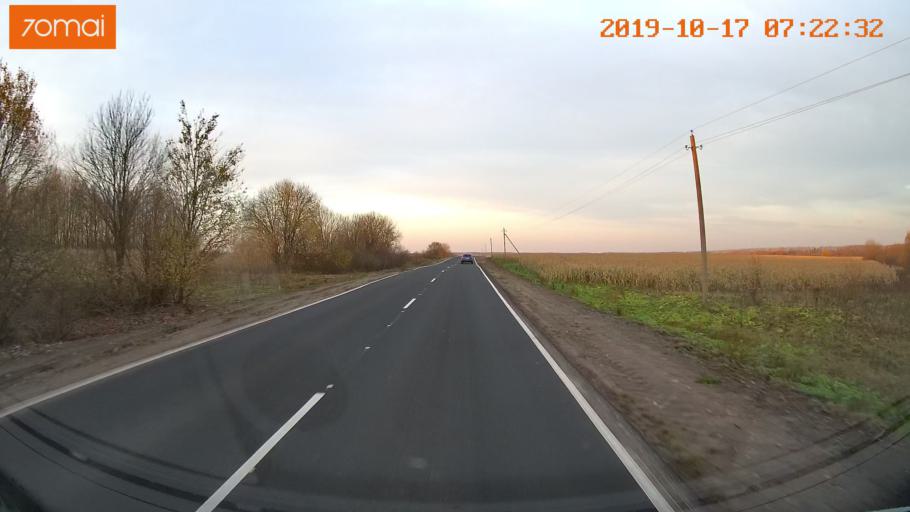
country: RU
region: Ivanovo
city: Gavrilov Posad
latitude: 56.3425
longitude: 40.1382
